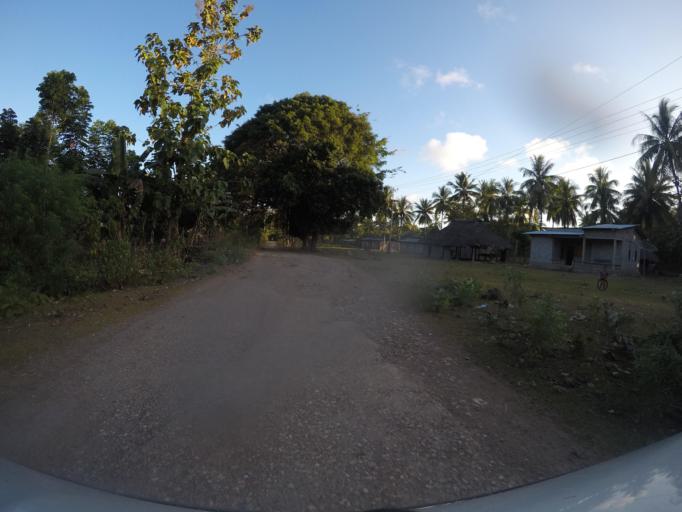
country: TL
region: Baucau
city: Venilale
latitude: -8.7375
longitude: 126.7146
